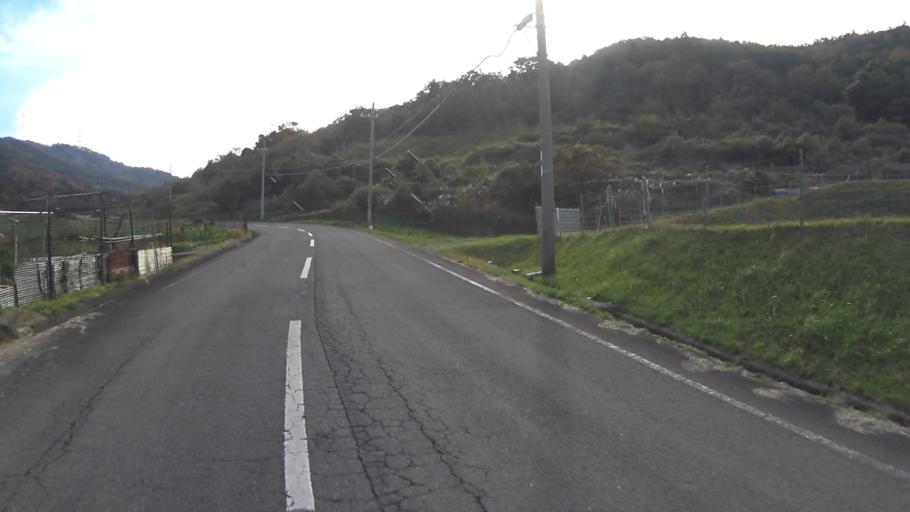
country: JP
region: Kyoto
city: Maizuru
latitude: 35.5526
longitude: 135.3958
